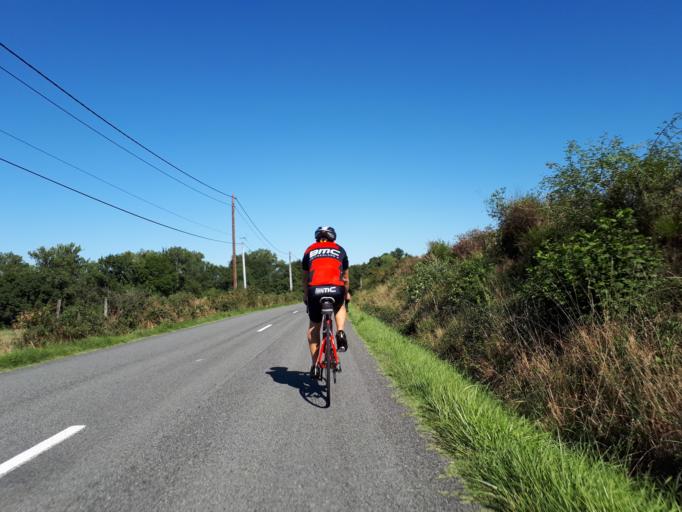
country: FR
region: Rhone-Alpes
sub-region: Departement de la Loire
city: Civens
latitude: 45.7831
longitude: 4.2459
